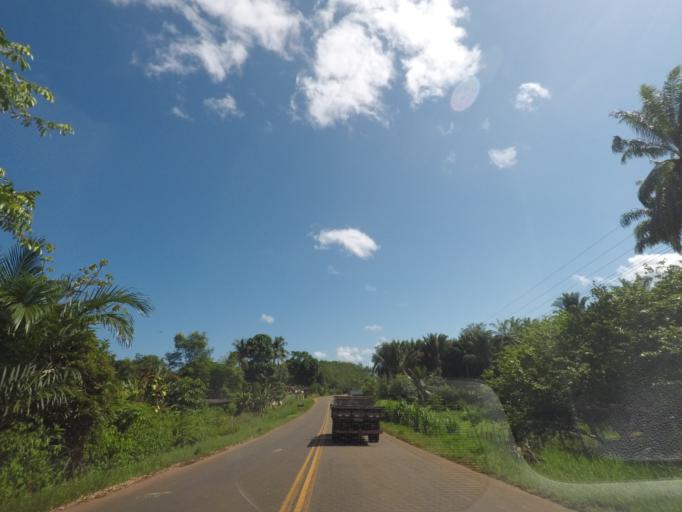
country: BR
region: Bahia
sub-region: Itubera
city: Itubera
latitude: -13.6944
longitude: -39.1332
